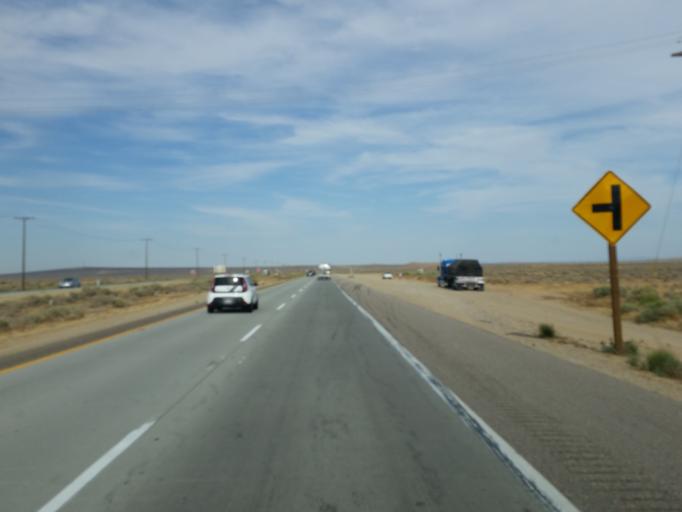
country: US
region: California
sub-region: Kern County
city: Mojave
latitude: 35.0296
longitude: -118.0890
